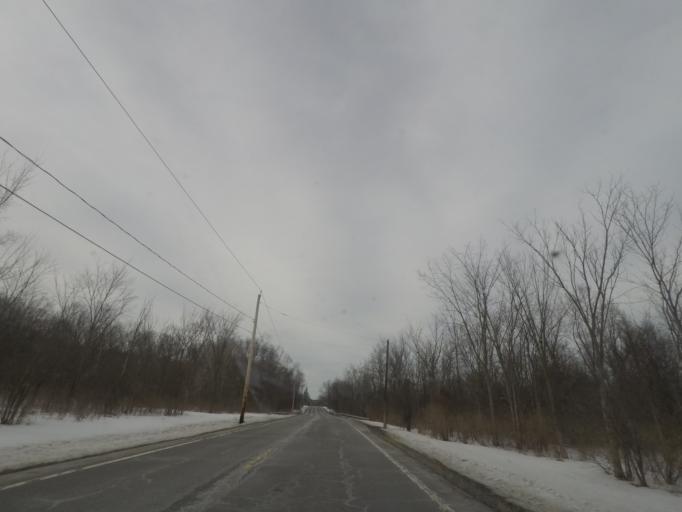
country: US
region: New York
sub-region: Albany County
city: Altamont
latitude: 42.6893
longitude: -74.0241
